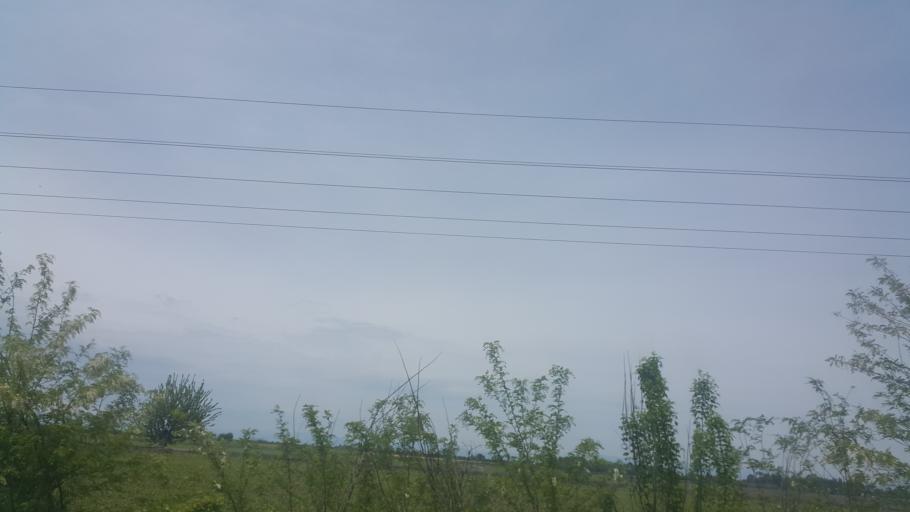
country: TR
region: Adana
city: Kosreli
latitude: 37.0683
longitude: 35.9945
